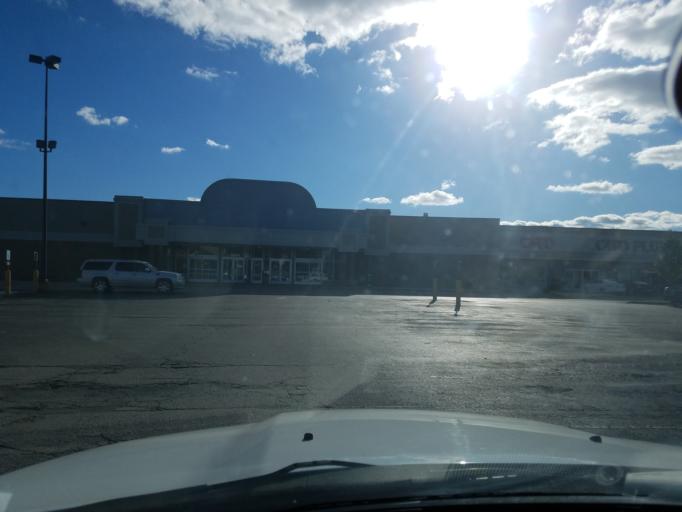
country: US
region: Kentucky
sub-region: Laurel County
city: London
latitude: 37.1067
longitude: -84.0885
